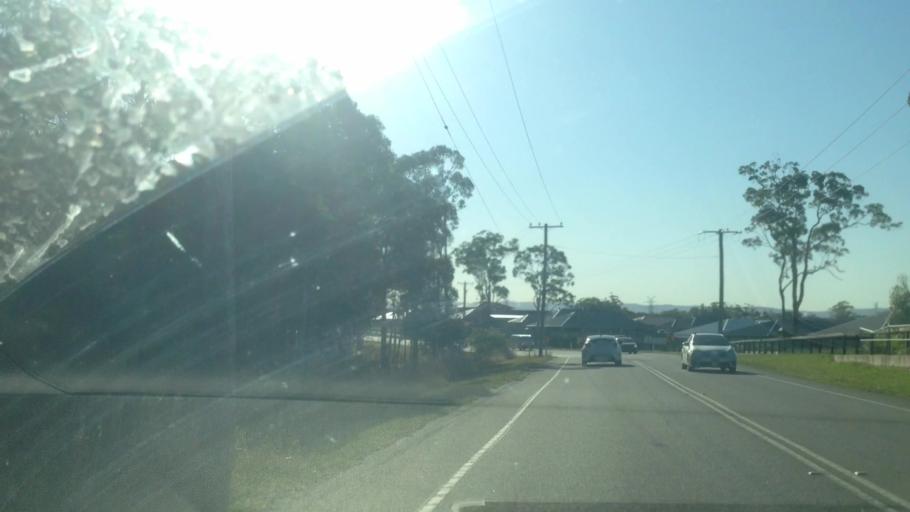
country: AU
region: New South Wales
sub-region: Lake Macquarie Shire
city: Dora Creek
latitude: -33.1112
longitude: 151.5087
